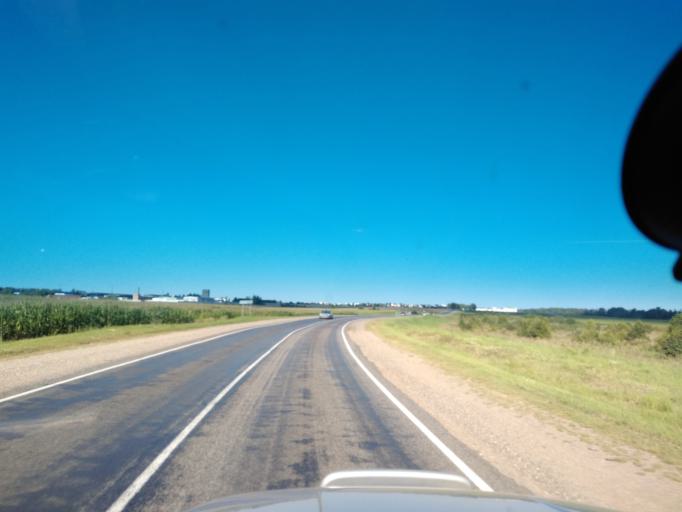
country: BY
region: Minsk
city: Dzyarzhynsk
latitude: 53.6670
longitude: 27.0905
